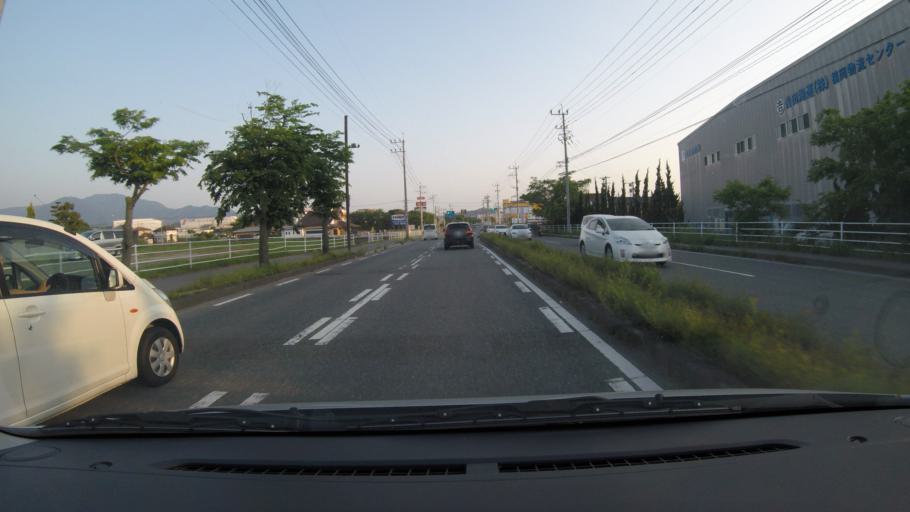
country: JP
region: Fukuoka
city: Sasaguri
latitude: 33.6430
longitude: 130.4960
